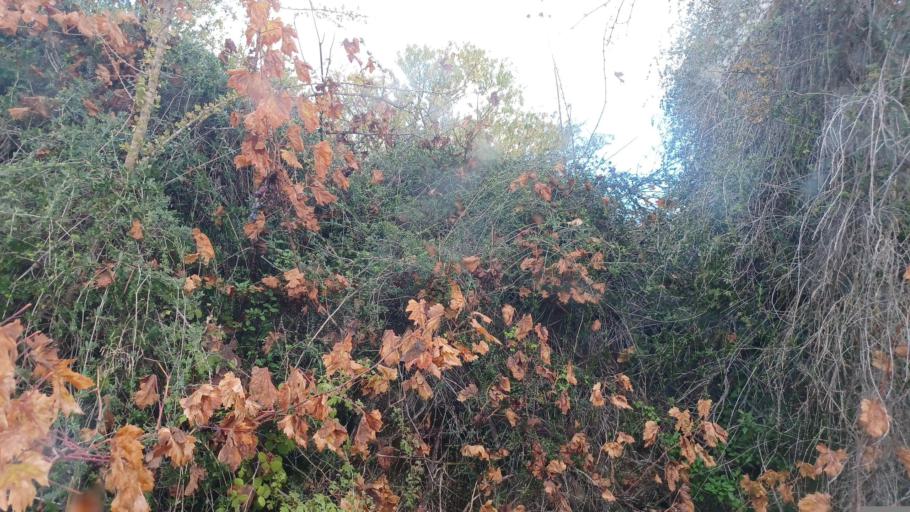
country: CY
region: Pafos
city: Mesogi
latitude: 34.8393
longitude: 32.5470
